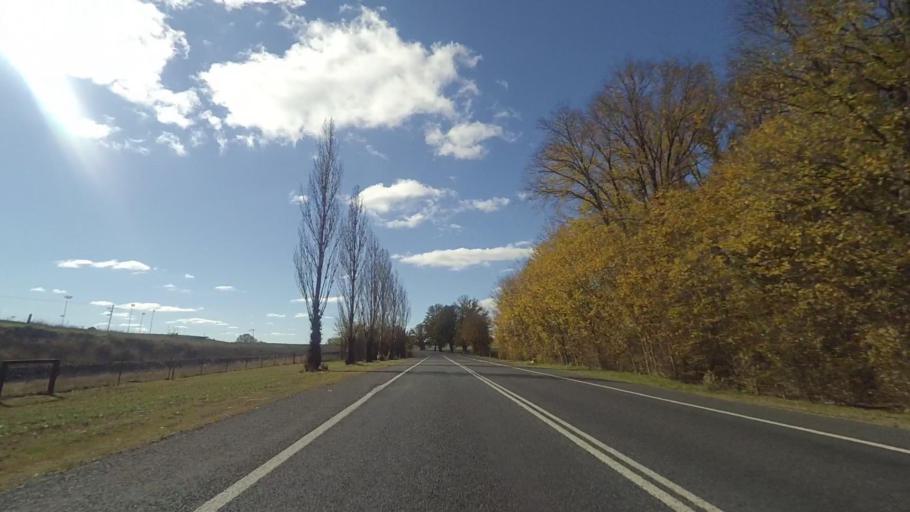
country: AU
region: New South Wales
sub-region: Bathurst Regional
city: Bathurst
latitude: -33.4538
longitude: 149.5768
